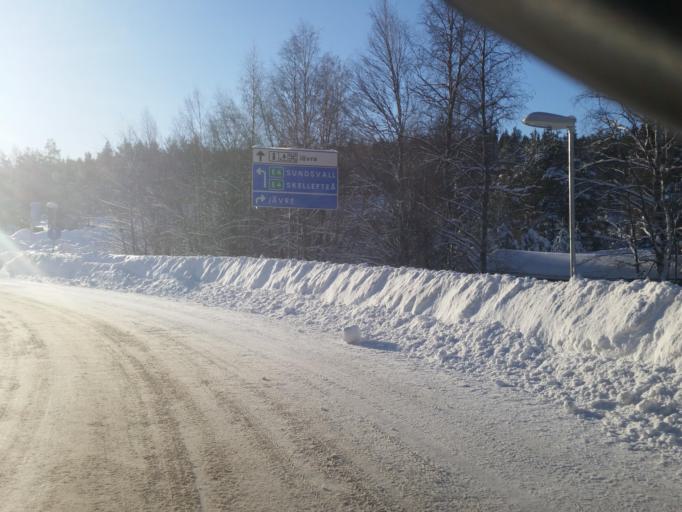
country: SE
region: Norrbotten
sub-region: Pitea Kommun
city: Pitea
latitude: 65.1443
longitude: 21.5016
